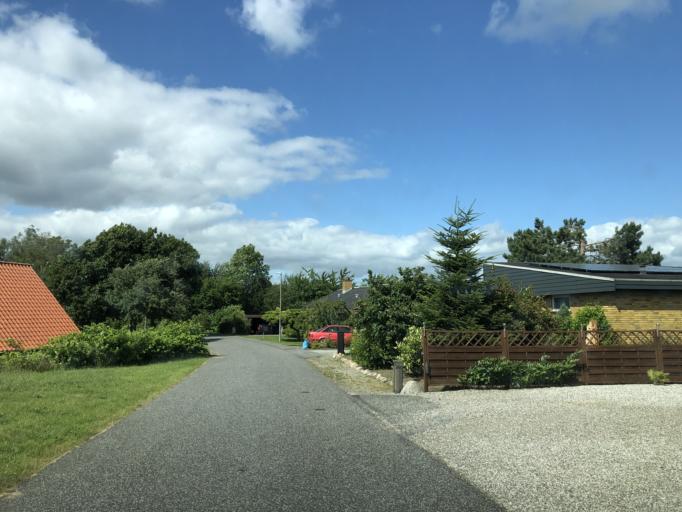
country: DK
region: South Denmark
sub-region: Vejle Kommune
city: Borkop
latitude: 55.5966
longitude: 9.6694
